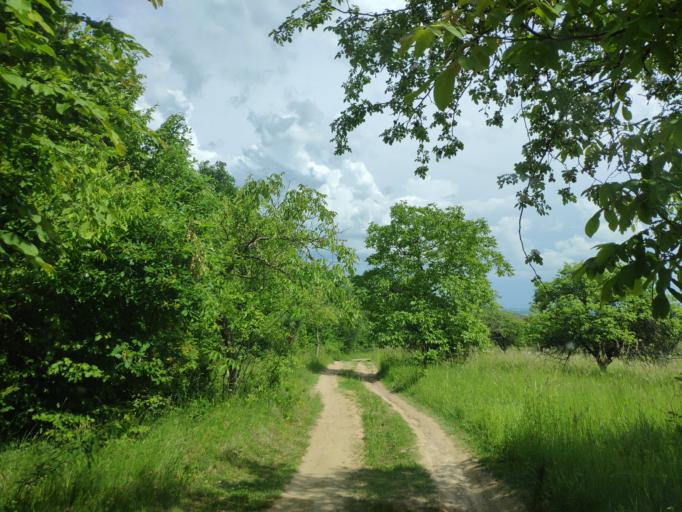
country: SK
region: Kosicky
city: Medzev
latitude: 48.7197
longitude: 20.9665
